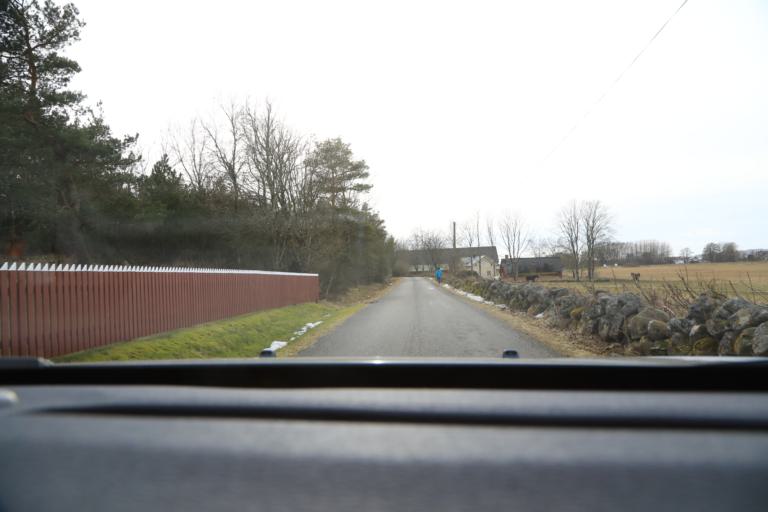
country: SE
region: Halland
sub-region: Varbergs Kommun
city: Veddige
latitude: 57.2173
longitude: 12.2322
